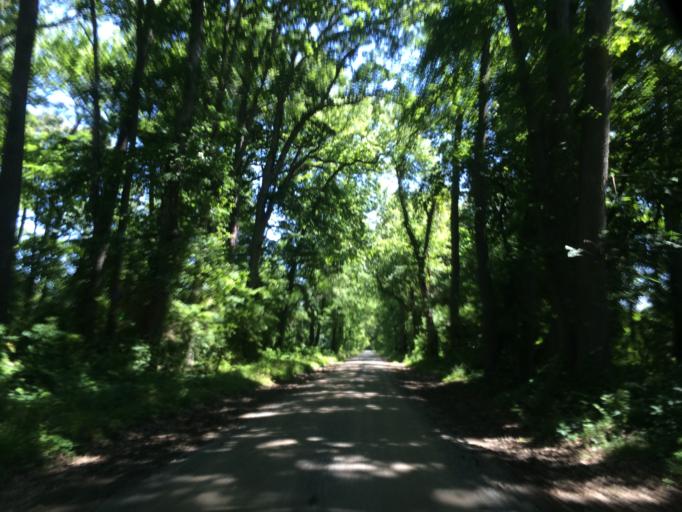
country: US
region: Maryland
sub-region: Queen Anne's County
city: Grasonville
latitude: 38.8936
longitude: -76.1562
